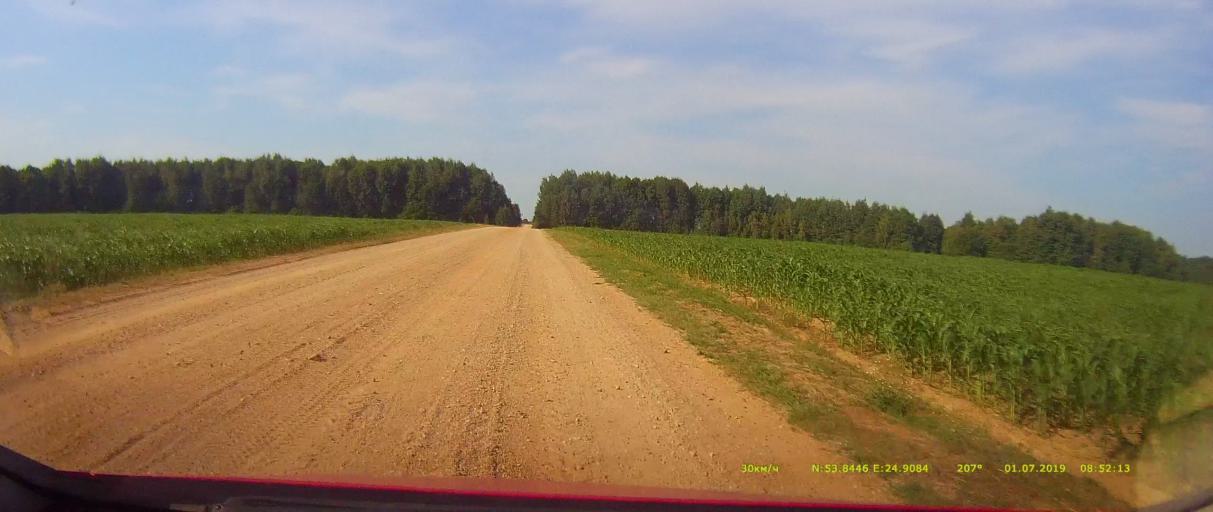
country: BY
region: Grodnenskaya
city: Shchuchin
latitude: 53.8447
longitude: 24.9085
